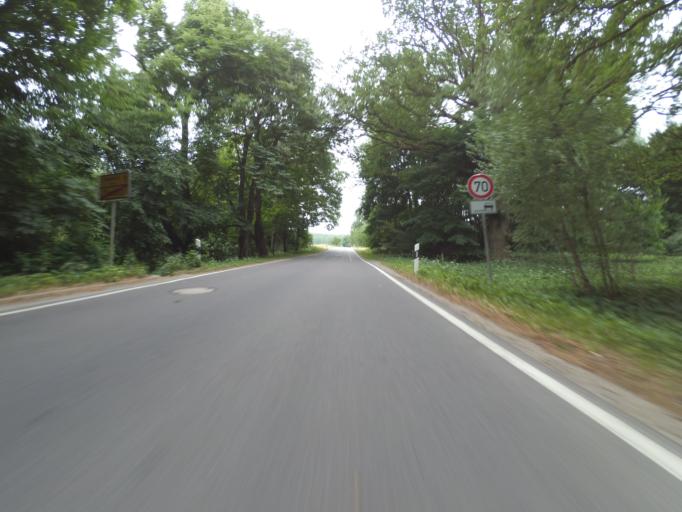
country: DE
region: Mecklenburg-Vorpommern
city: Krakow am See
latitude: 53.6304
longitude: 12.3468
